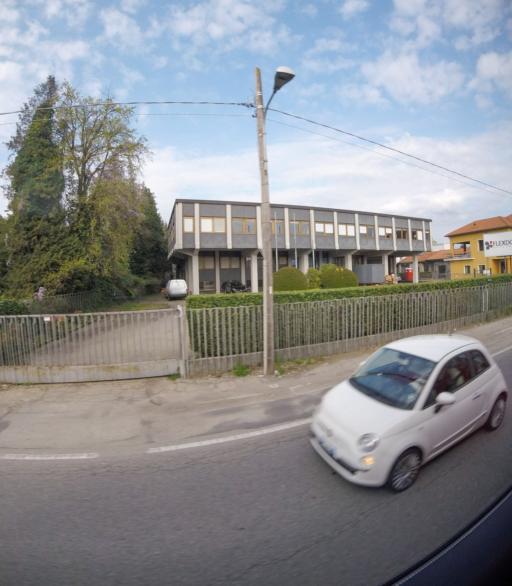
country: IT
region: Piedmont
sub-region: Provincia di Novara
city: Gozzano
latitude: 45.7389
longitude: 8.4390
